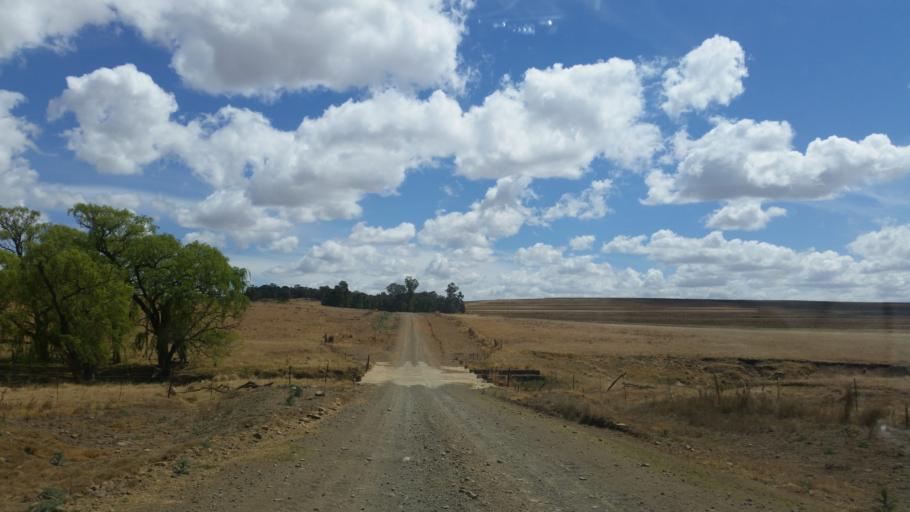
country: ZA
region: Orange Free State
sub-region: Thabo Mofutsanyana District Municipality
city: Bethlehem
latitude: -28.1917
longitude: 28.5886
